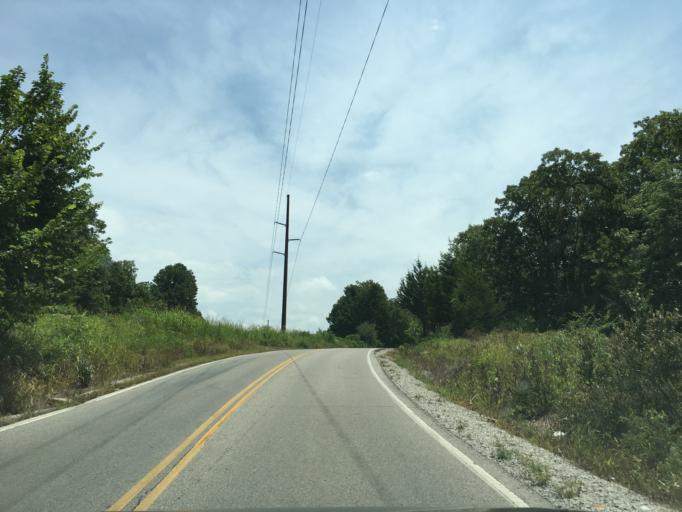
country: US
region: Oklahoma
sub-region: Tulsa County
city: Jenks
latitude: 36.0752
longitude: -96.0012
